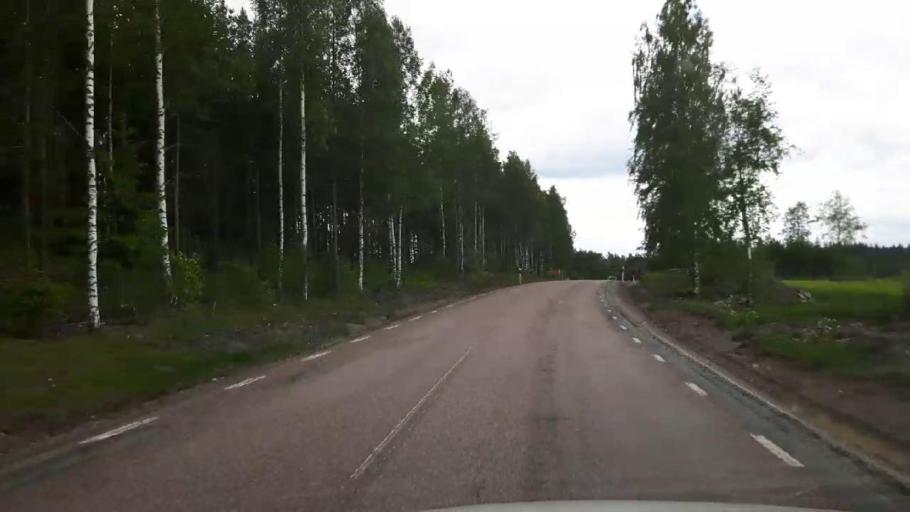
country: SE
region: Vaestmanland
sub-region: Skinnskattebergs Kommun
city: Skinnskatteberg
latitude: 59.8423
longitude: 15.8406
